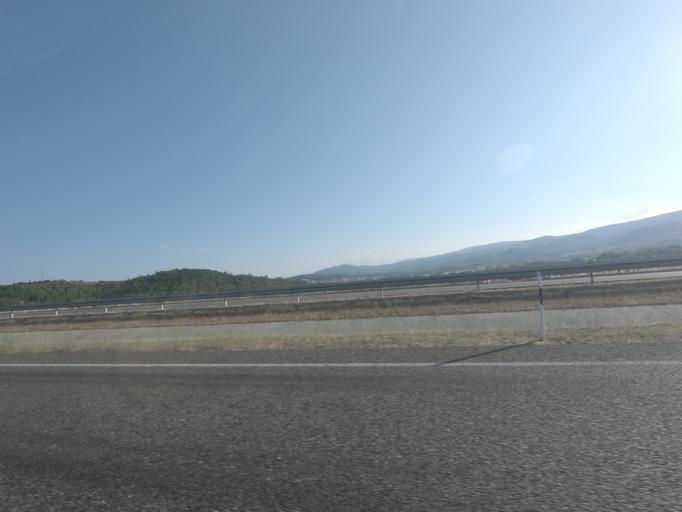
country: ES
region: Galicia
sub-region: Provincia de Ourense
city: Oimbra
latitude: 41.8637
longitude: -7.4280
